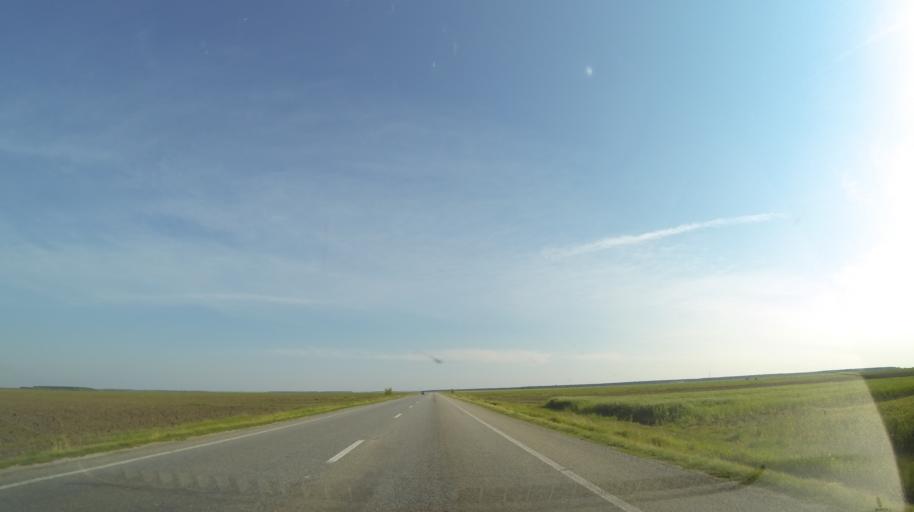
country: RO
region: Olt
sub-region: Comuna Scornicesti
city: Negreni
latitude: 44.5831
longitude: 24.6058
